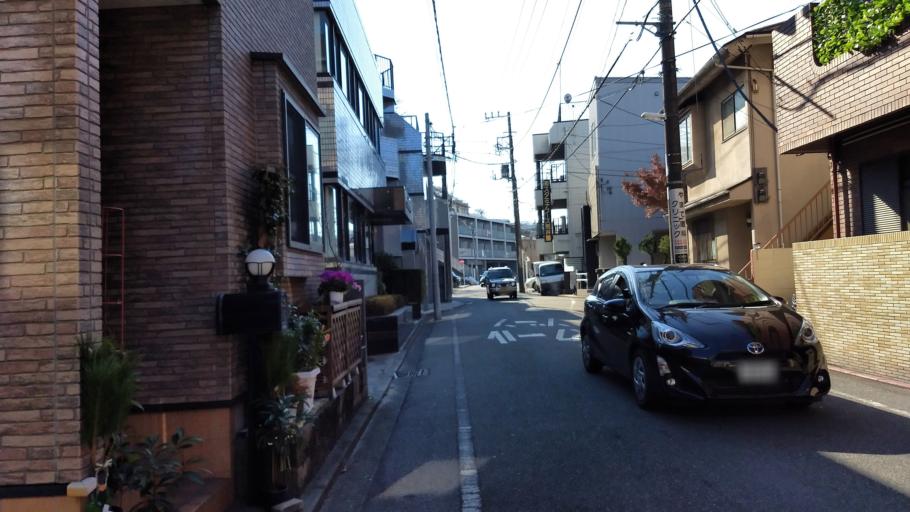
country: JP
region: Kanagawa
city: Yokohama
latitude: 35.4307
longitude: 139.6489
